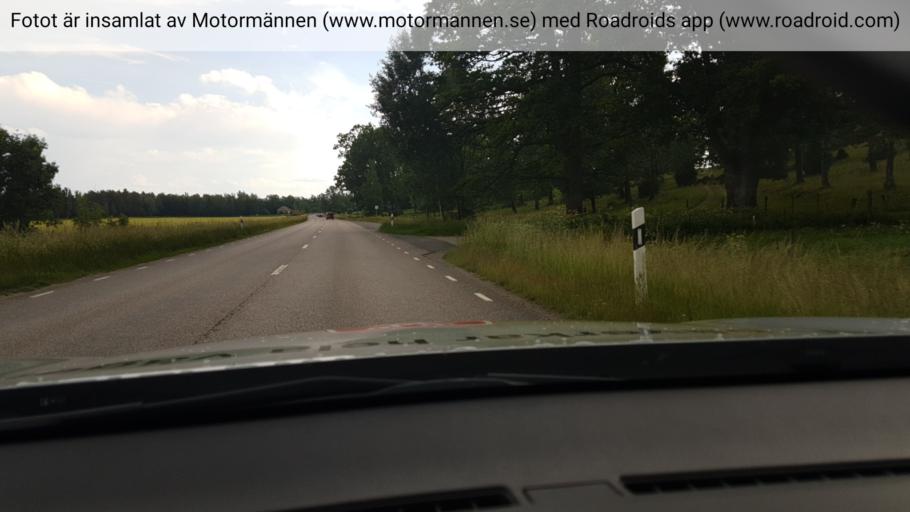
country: SE
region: Vaestra Goetaland
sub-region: Hjo Kommun
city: Hjo
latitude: 58.1422
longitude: 14.2167
